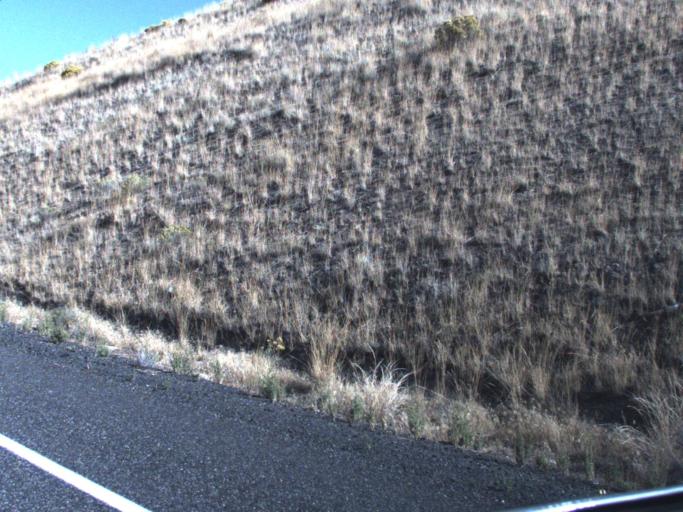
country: US
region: Washington
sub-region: Benton County
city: Highland
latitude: 46.1544
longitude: -119.1680
